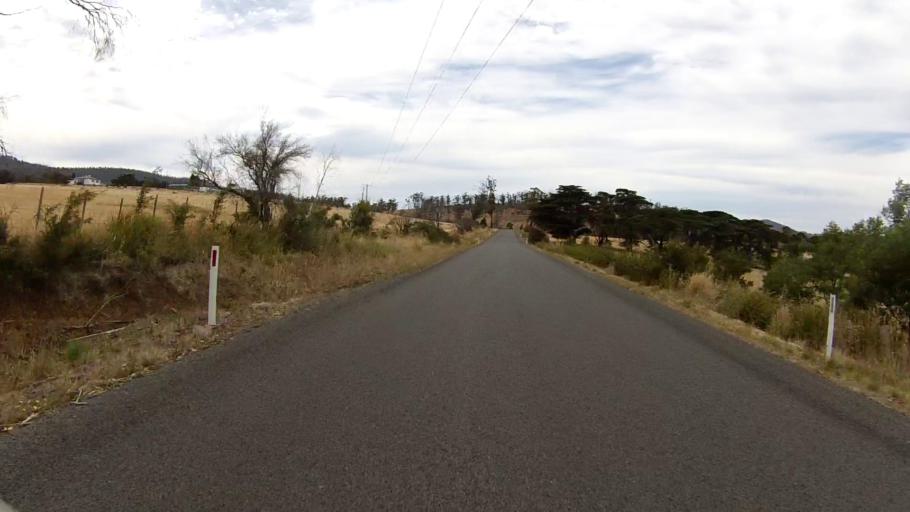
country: AU
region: Tasmania
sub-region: Sorell
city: Sorell
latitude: -42.8966
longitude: 147.7711
